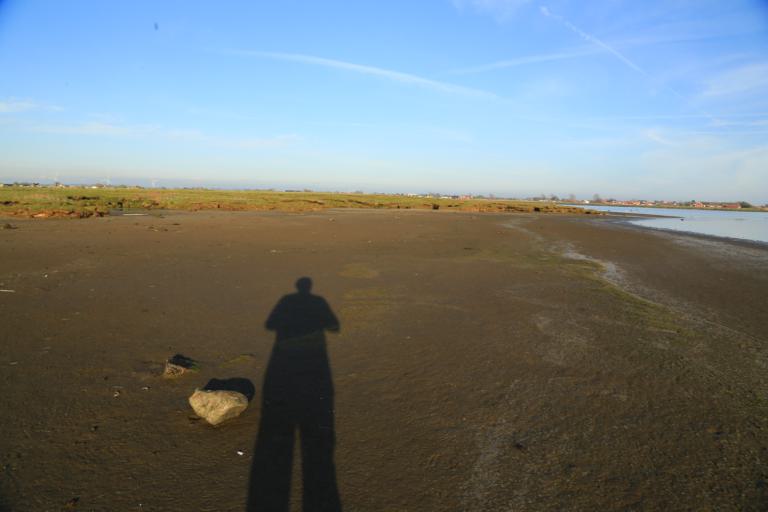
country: SE
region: Halland
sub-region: Varbergs Kommun
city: Traslovslage
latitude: 57.0346
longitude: 12.3090
